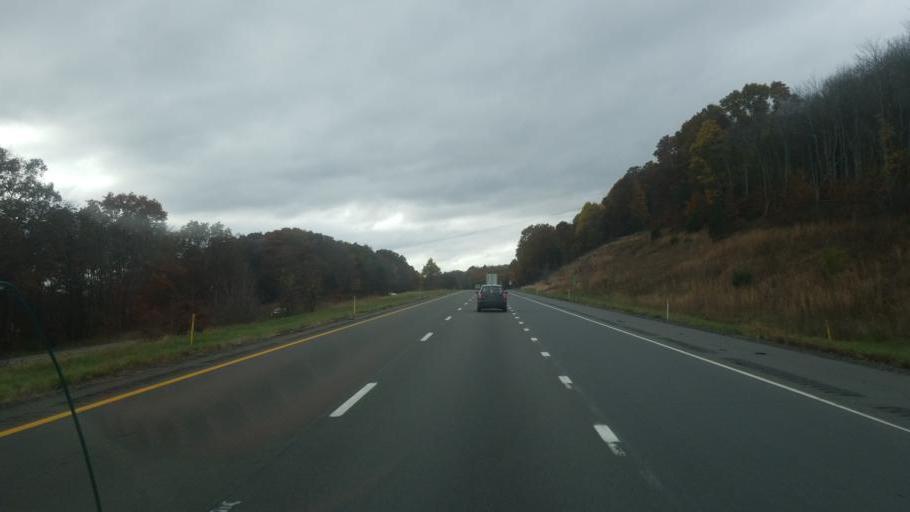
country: US
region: Pennsylvania
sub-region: Clarion County
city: Marianne
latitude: 41.1948
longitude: -79.4334
